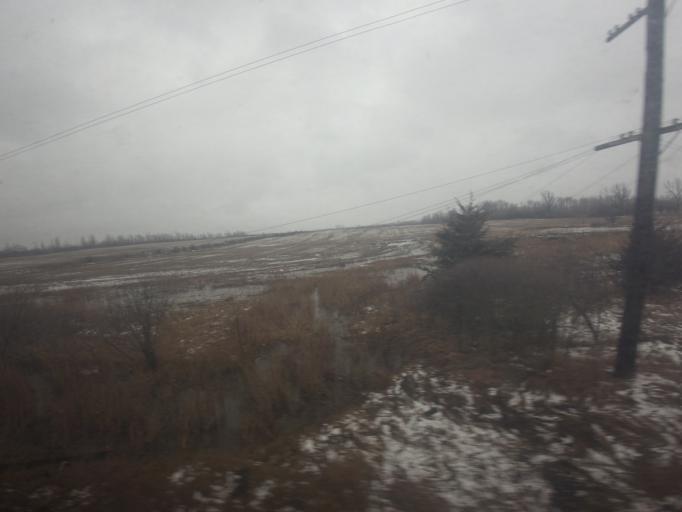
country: CA
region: Ontario
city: Deseronto
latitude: 44.2218
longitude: -77.1375
